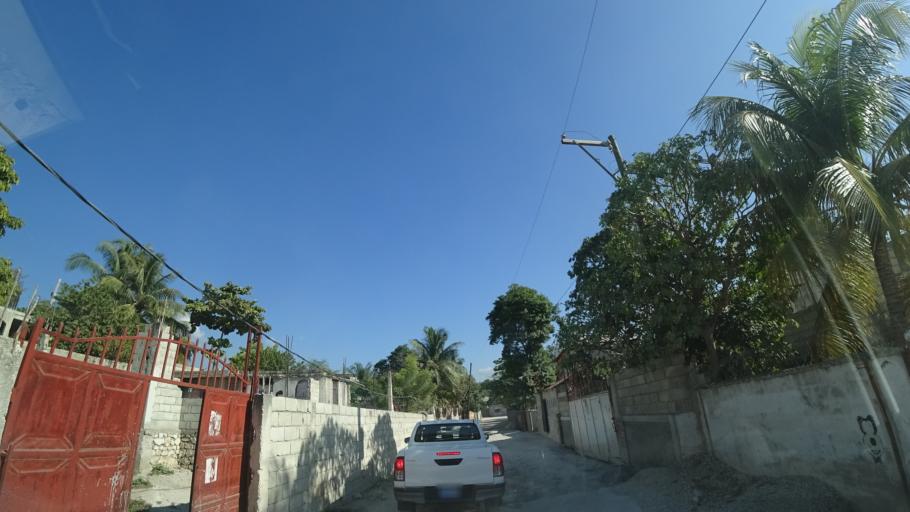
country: HT
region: Ouest
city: Delmas 73
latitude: 18.5565
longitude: -72.2834
